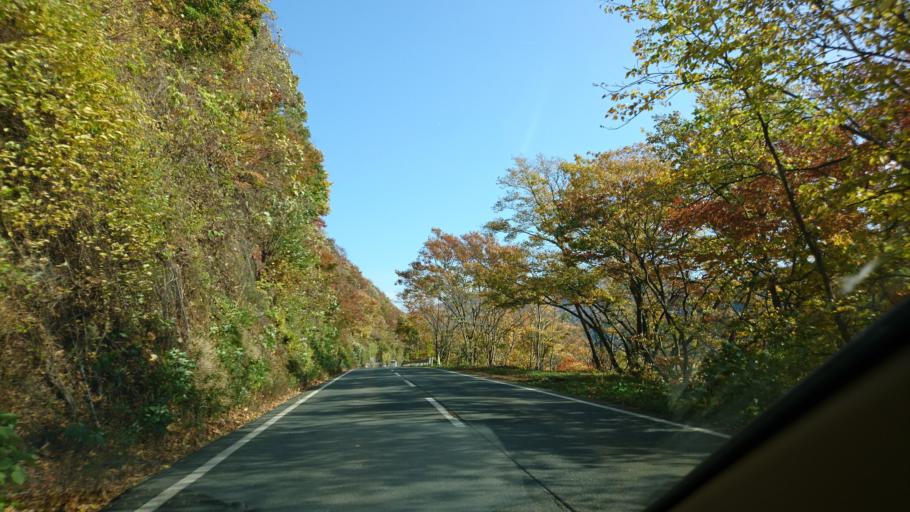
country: JP
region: Iwate
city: Kitakami
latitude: 39.3075
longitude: 140.8510
